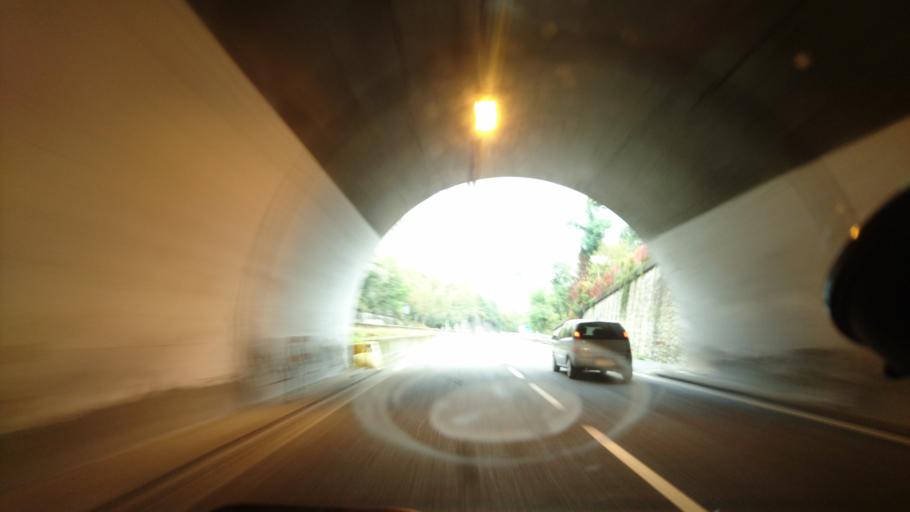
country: IT
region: Piedmont
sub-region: Provincia Verbano-Cusio-Ossola
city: Baveno
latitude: 45.9100
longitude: 8.4878
